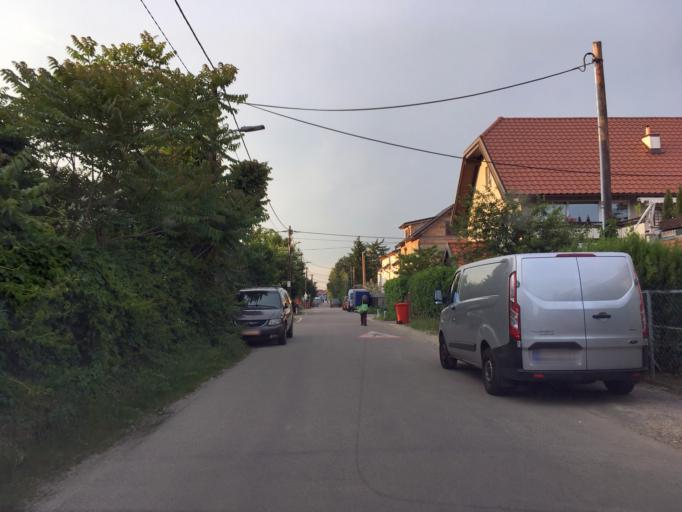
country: AT
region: Lower Austria
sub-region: Politischer Bezirk Wien-Umgebung
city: Gerasdorf bei Wien
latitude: 48.3134
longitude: 16.4942
